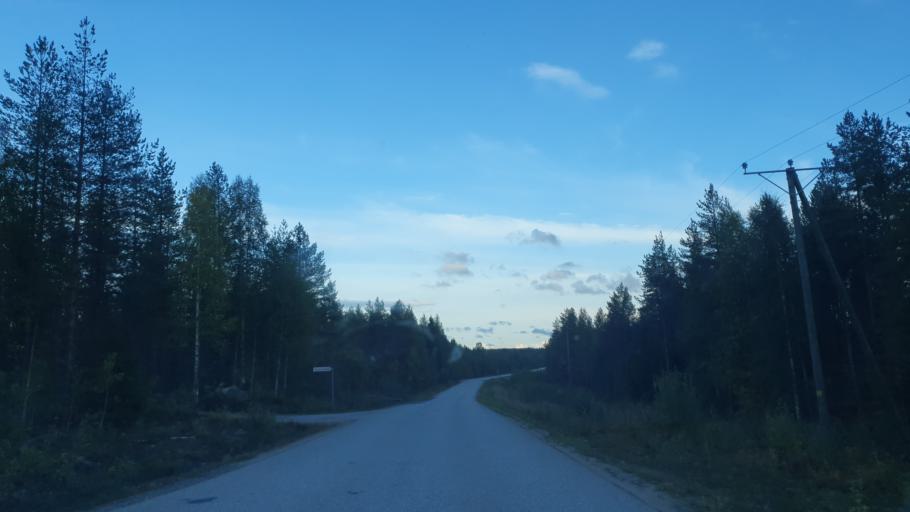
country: FI
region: Kainuu
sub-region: Kehys-Kainuu
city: Kuhmo
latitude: 64.4179
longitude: 29.9263
